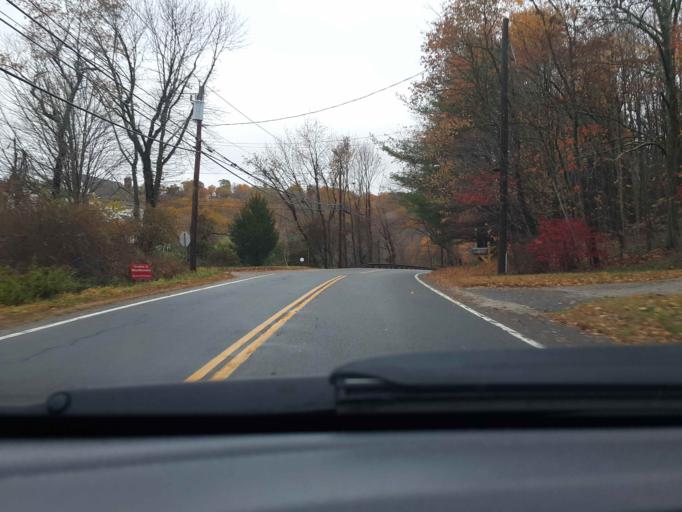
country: US
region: Connecticut
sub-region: New Haven County
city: North Branford
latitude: 41.3592
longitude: -72.7217
